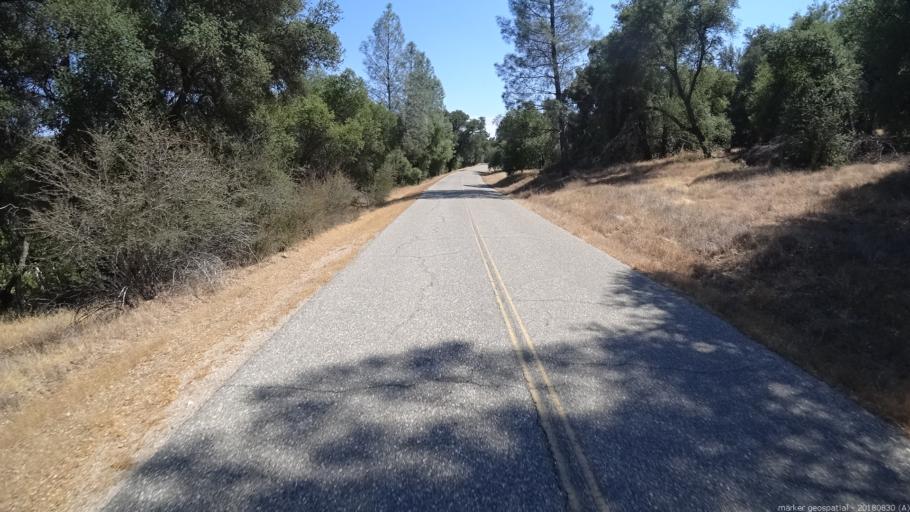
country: US
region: California
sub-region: Monterey County
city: King City
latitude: 36.0674
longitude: -121.3151
